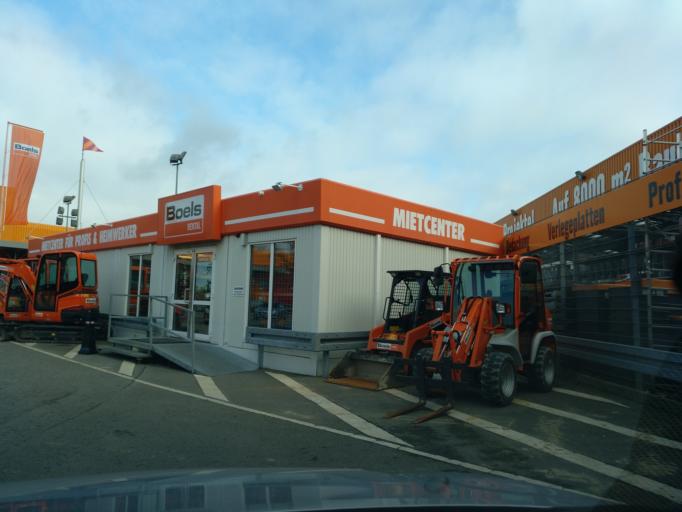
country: DE
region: Berlin
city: Altglienicke
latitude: 52.3971
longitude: 13.5443
